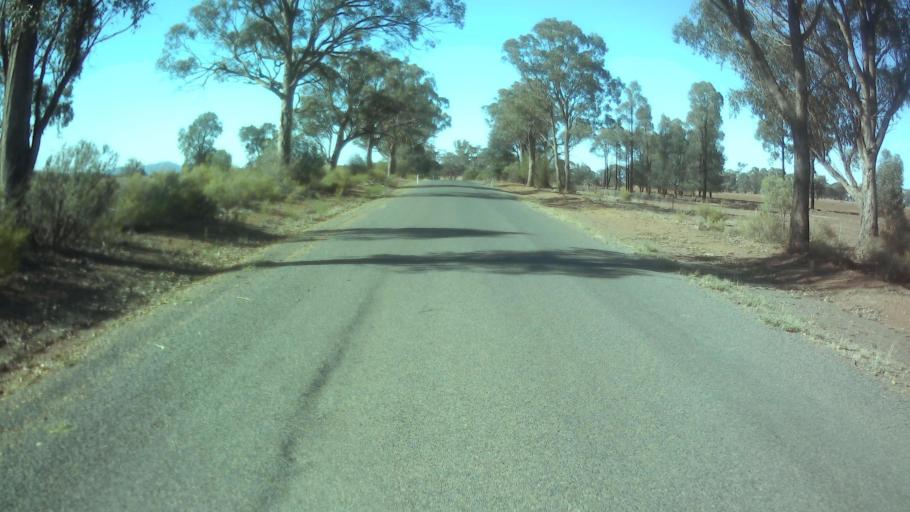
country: AU
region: New South Wales
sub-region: Forbes
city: Forbes
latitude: -33.6983
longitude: 147.8071
